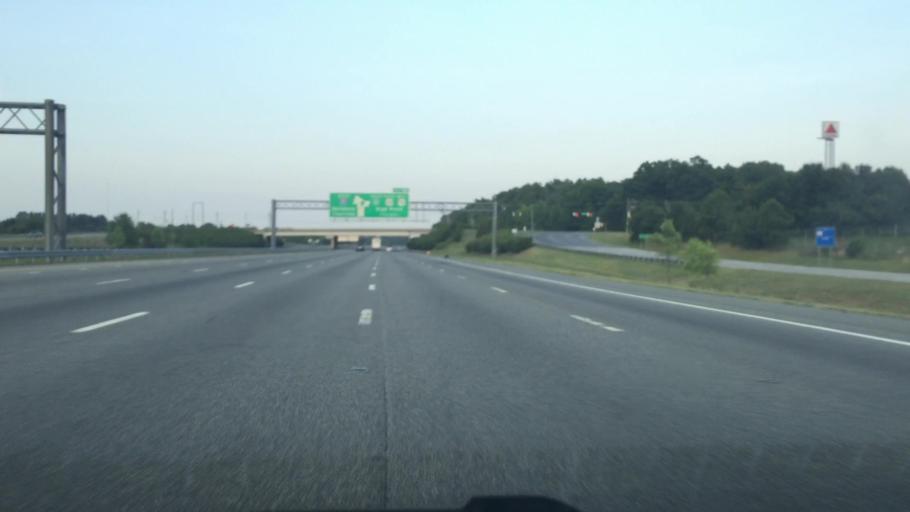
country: US
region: North Carolina
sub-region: Guilford County
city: Jamestown
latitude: 35.9998
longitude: -79.8621
